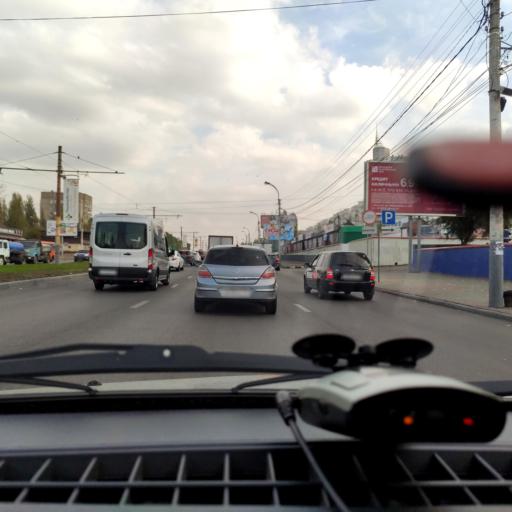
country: RU
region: Voronezj
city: Voronezh
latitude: 51.6878
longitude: 39.2553
